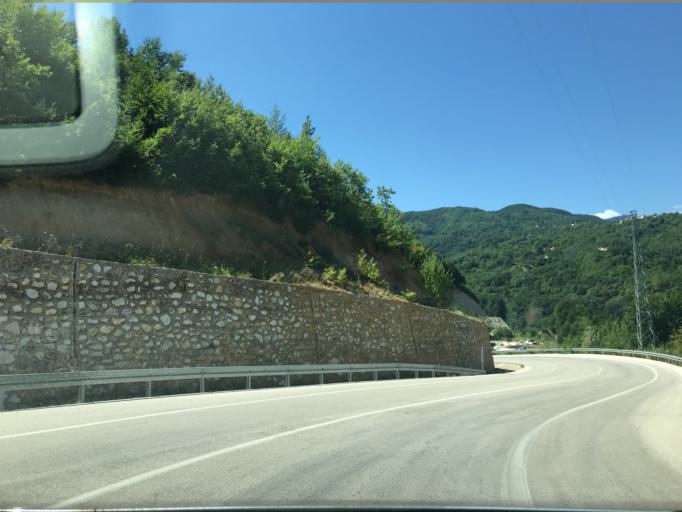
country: TR
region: Bursa
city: Tahtakopru
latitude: 39.9402
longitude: 29.5924
